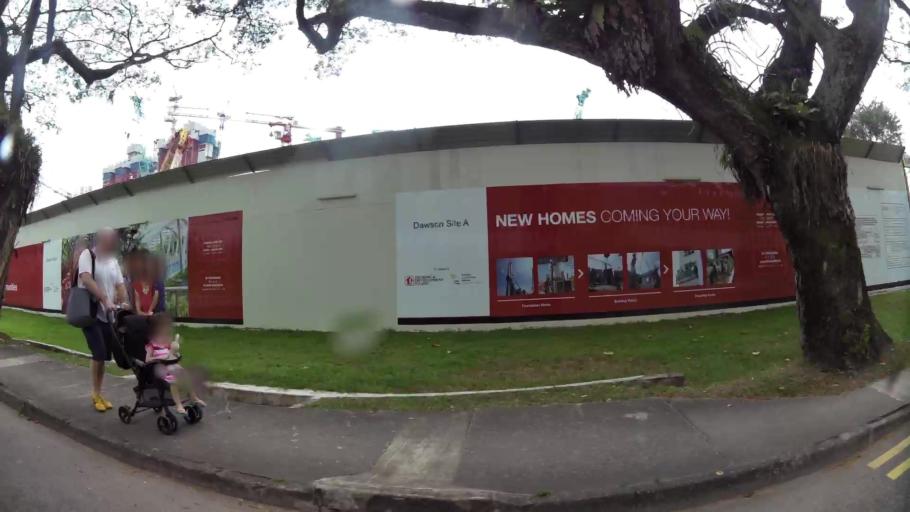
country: SG
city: Singapore
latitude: 1.2984
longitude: 103.8052
